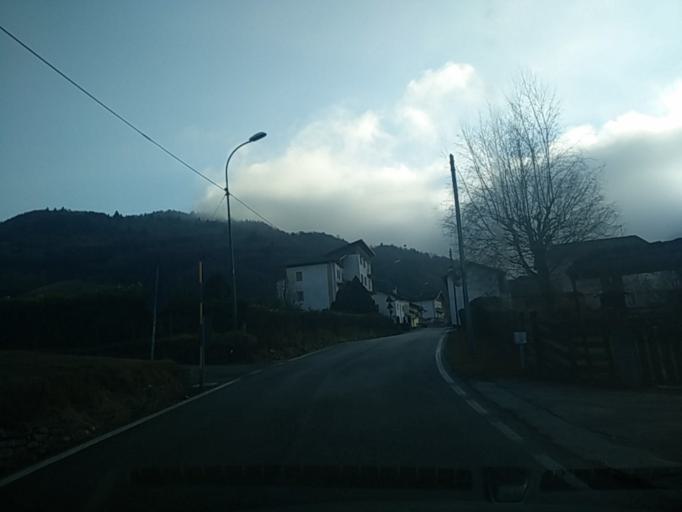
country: IT
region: Veneto
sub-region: Provincia di Belluno
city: Trichiana
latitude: 46.0325
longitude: 12.1634
